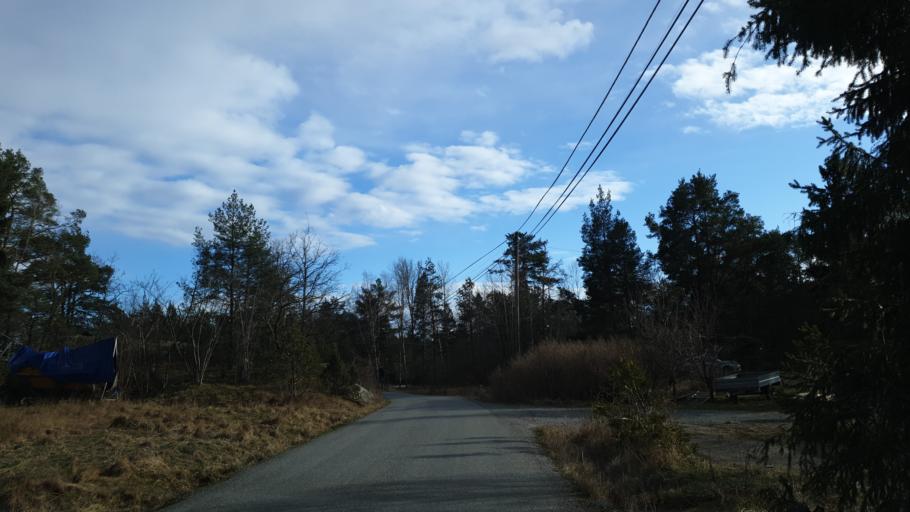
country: SE
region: Stockholm
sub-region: Varmdo Kommun
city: Holo
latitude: 59.3695
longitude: 18.6702
